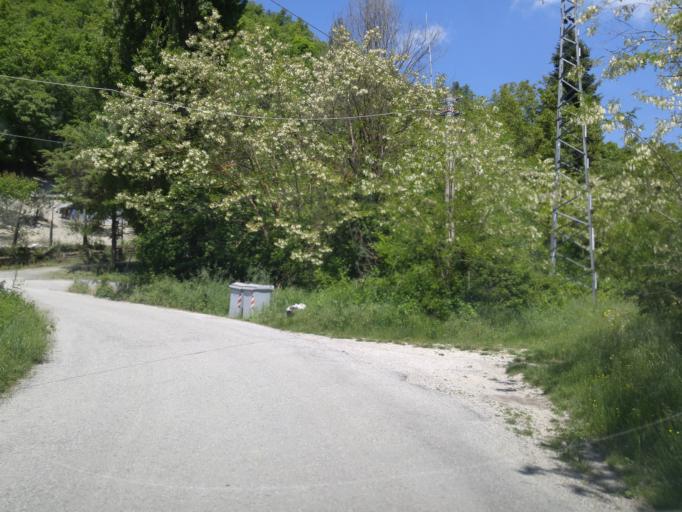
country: IT
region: The Marches
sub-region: Provincia di Pesaro e Urbino
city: Fermignano
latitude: 43.7149
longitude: 12.6751
